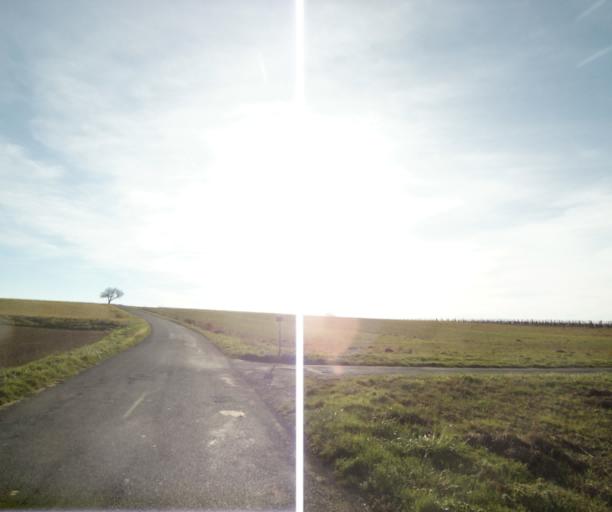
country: FR
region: Poitou-Charentes
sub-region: Departement de la Charente-Maritime
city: Chaniers
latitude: 45.7307
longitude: -0.5498
